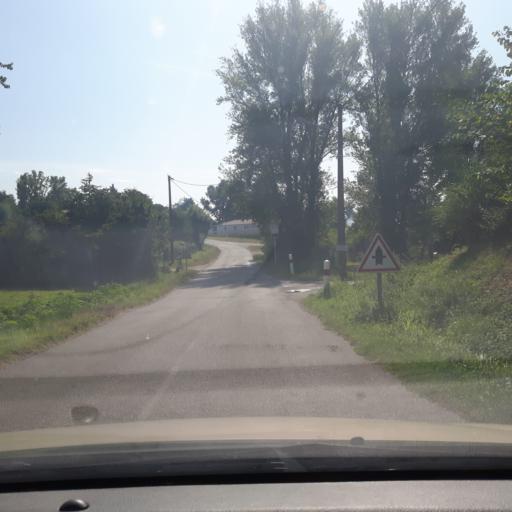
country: FR
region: Midi-Pyrenees
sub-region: Departement de la Haute-Garonne
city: Villeneuve-les-Bouloc
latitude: 43.7674
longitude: 1.4156
